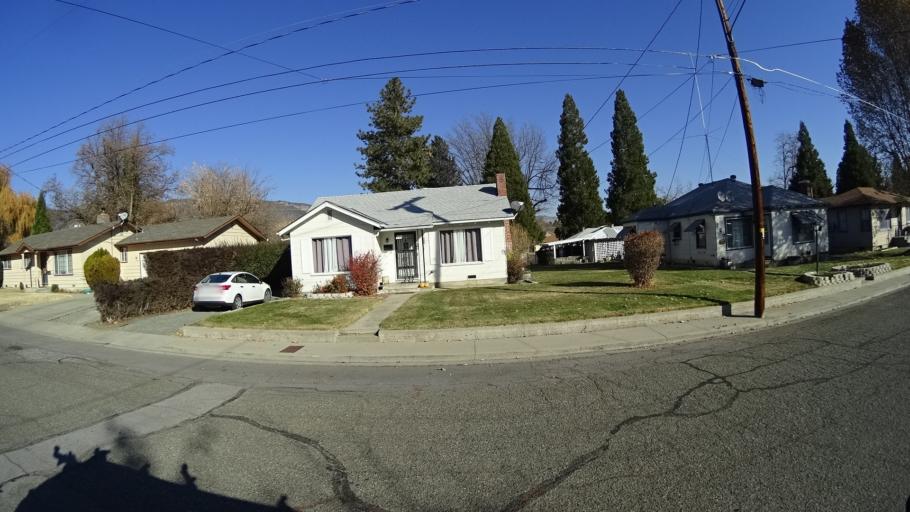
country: US
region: California
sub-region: Siskiyou County
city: Yreka
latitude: 41.7308
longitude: -122.6455
